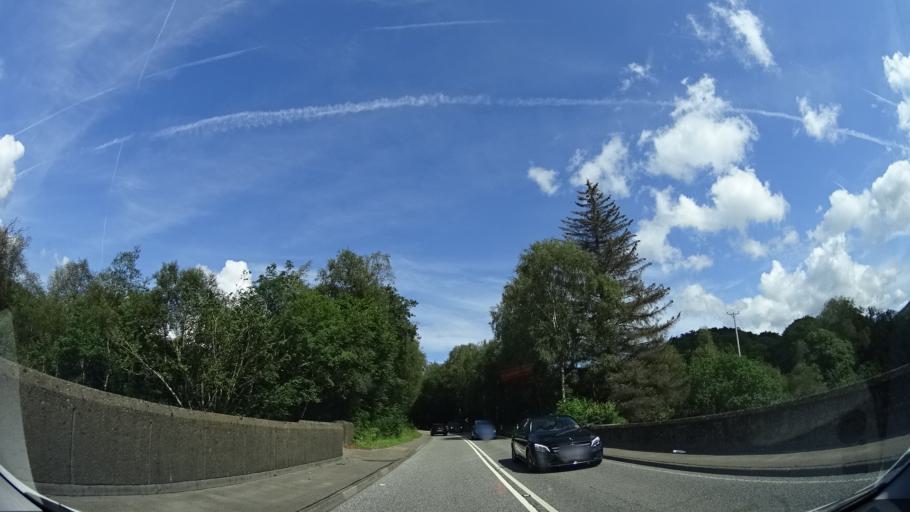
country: GB
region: Scotland
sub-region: Highland
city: Fort William
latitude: 56.7729
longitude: -5.1667
